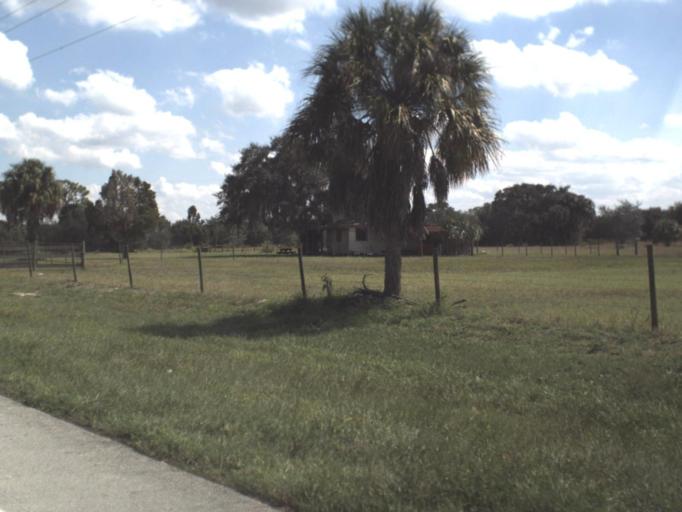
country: US
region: Florida
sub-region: Highlands County
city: Sebring
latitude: 27.4124
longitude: -81.5099
